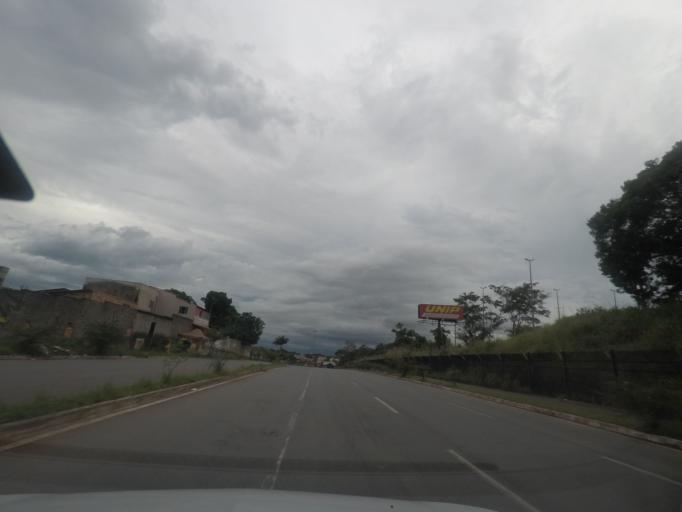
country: BR
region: Goias
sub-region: Goiania
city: Goiania
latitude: -16.7206
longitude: -49.2344
